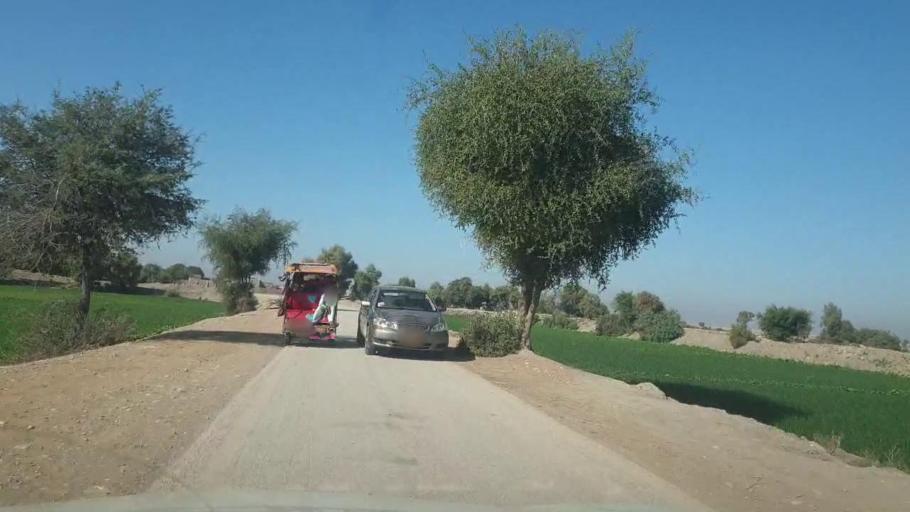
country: PK
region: Sindh
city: Bhan
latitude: 26.5554
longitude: 67.6325
